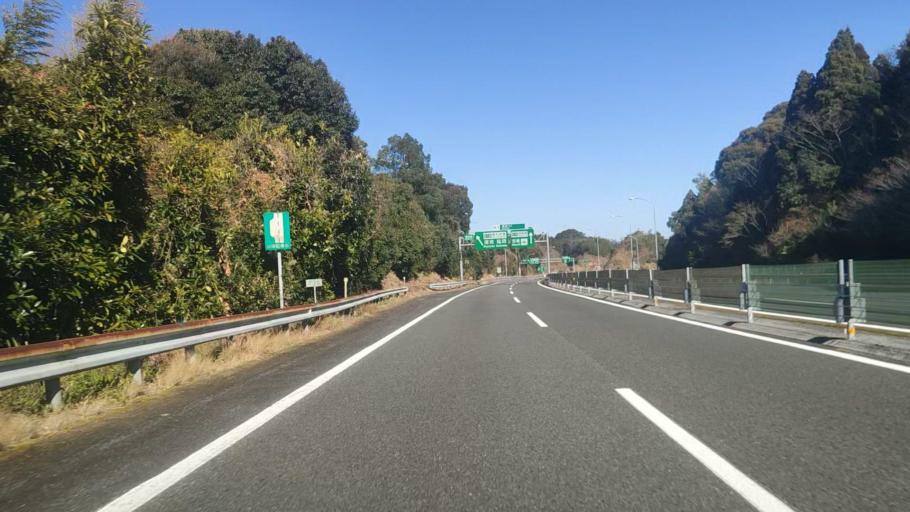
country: JP
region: Miyazaki
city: Miyazaki-shi
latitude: 31.8446
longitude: 131.3523
